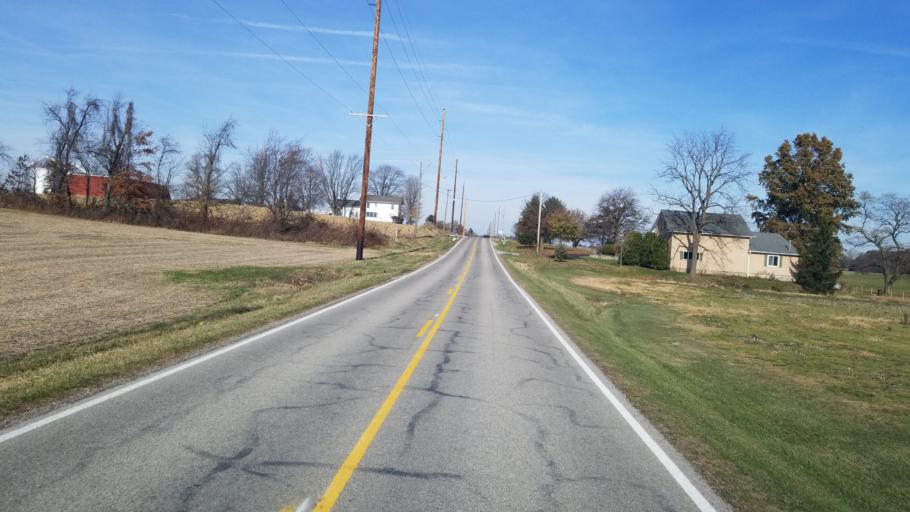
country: US
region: Ohio
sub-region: Huron County
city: Monroeville
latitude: 41.1728
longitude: -82.6834
